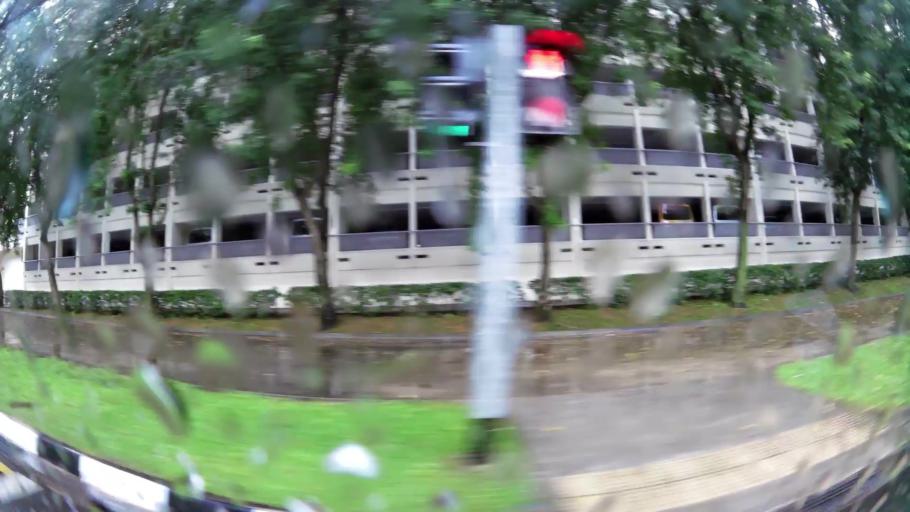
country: MY
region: Johor
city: Kampung Pasir Gudang Baru
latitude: 1.3819
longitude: 103.8998
